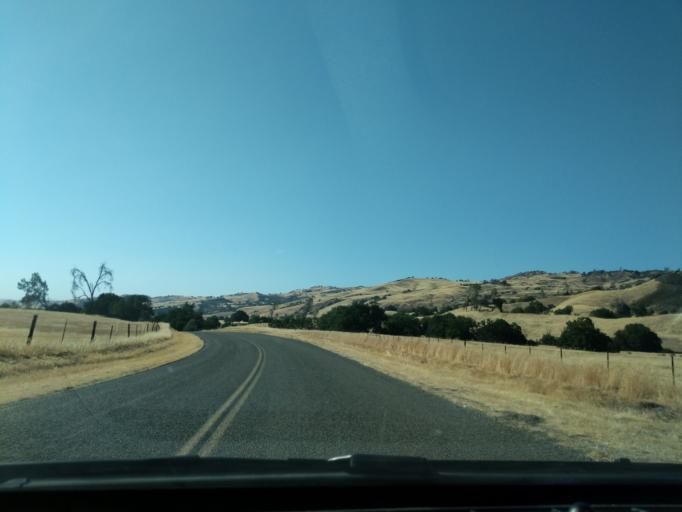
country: US
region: California
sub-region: Monterey County
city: King City
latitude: 36.1652
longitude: -120.7771
